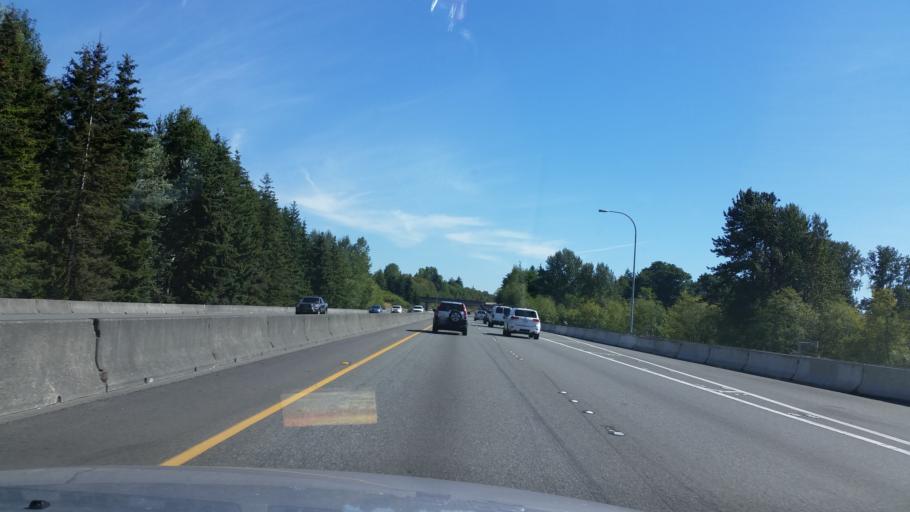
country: US
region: Washington
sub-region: King County
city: Normandy Park
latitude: 47.4487
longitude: -122.3230
